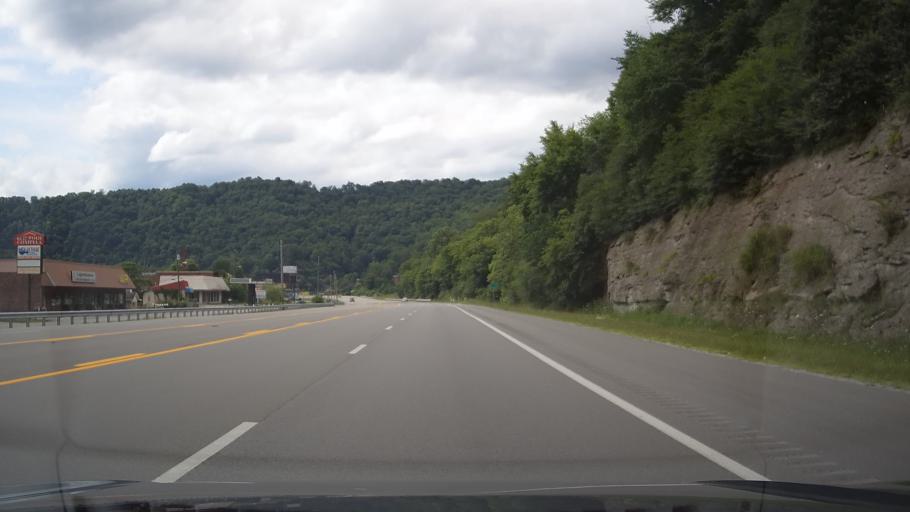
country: US
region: Kentucky
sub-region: Pike County
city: Coal Run Village
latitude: 37.5357
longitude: -82.5792
